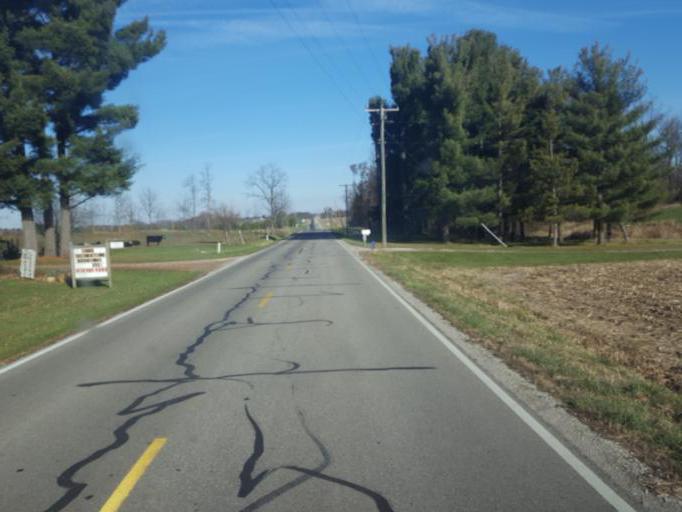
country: US
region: Ohio
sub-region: Crawford County
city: Crestline
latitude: 40.8840
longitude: -82.7724
